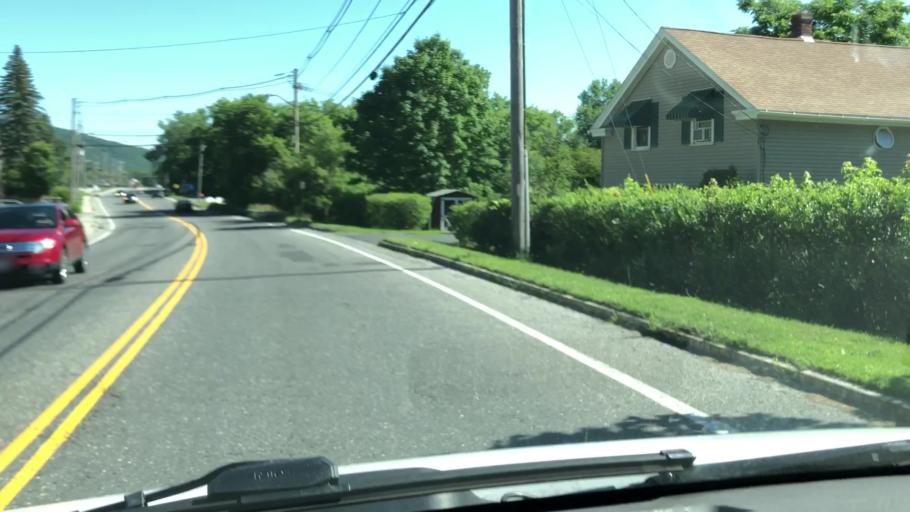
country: US
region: Massachusetts
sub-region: Berkshire County
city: Adams
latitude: 42.6392
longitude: -73.1123
